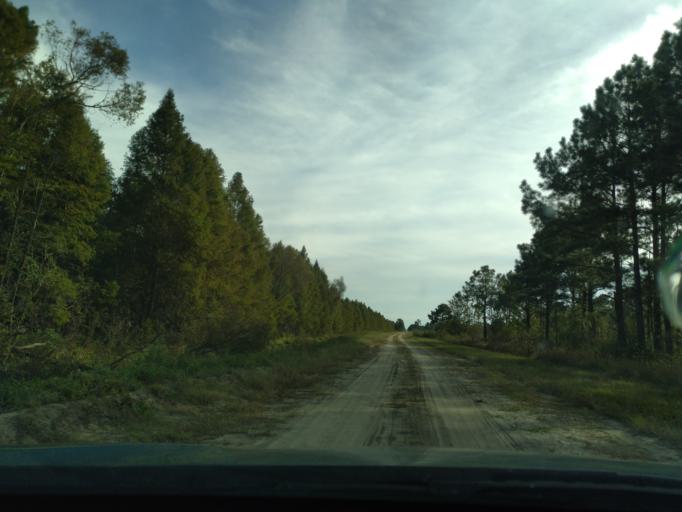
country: US
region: North Carolina
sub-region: Beaufort County
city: Belhaven
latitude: 35.6837
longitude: -76.5446
